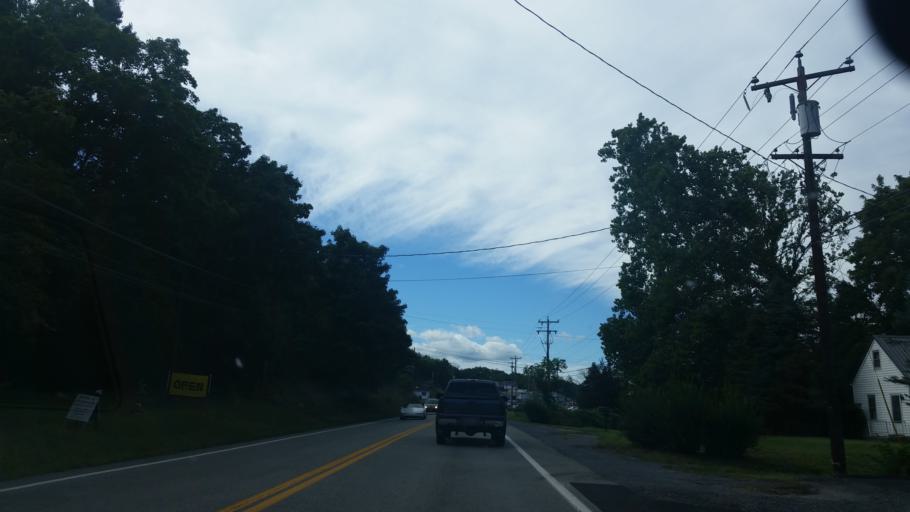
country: US
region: West Virginia
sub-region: Morgan County
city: Berkeley Springs
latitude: 39.6088
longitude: -78.2371
